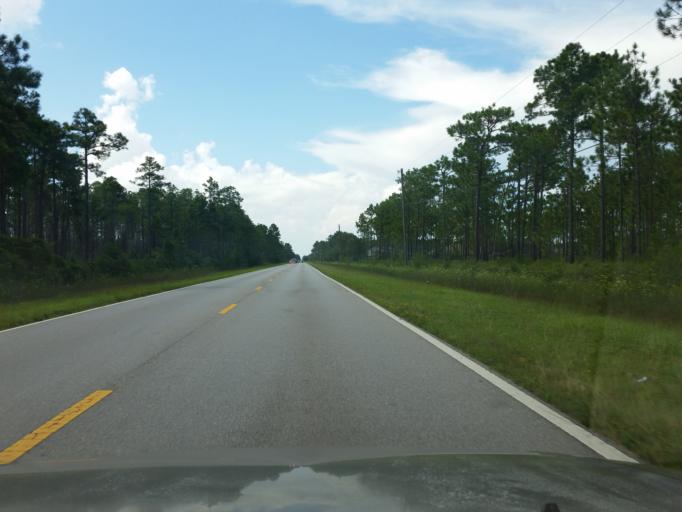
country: US
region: Florida
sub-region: Escambia County
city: Myrtle Grove
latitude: 30.3690
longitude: -87.4025
